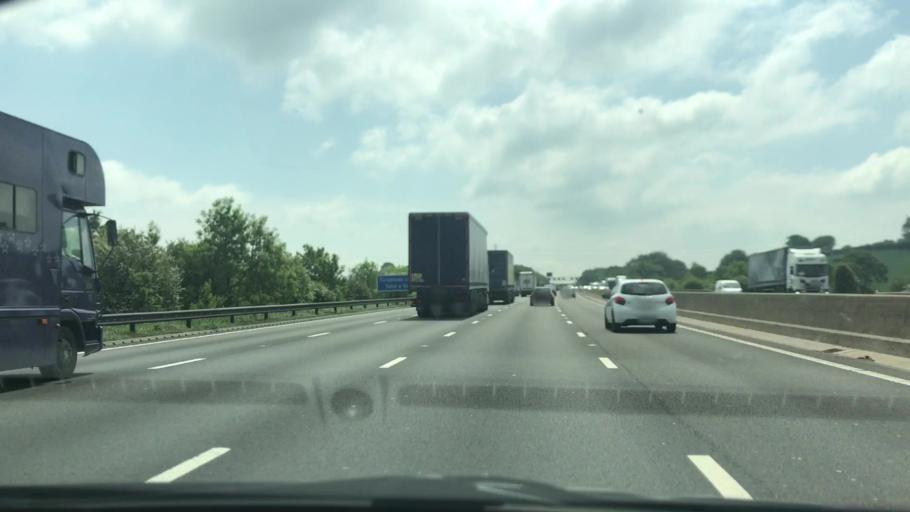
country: GB
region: England
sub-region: Derbyshire
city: Tibshelf
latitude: 53.1595
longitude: -1.3251
